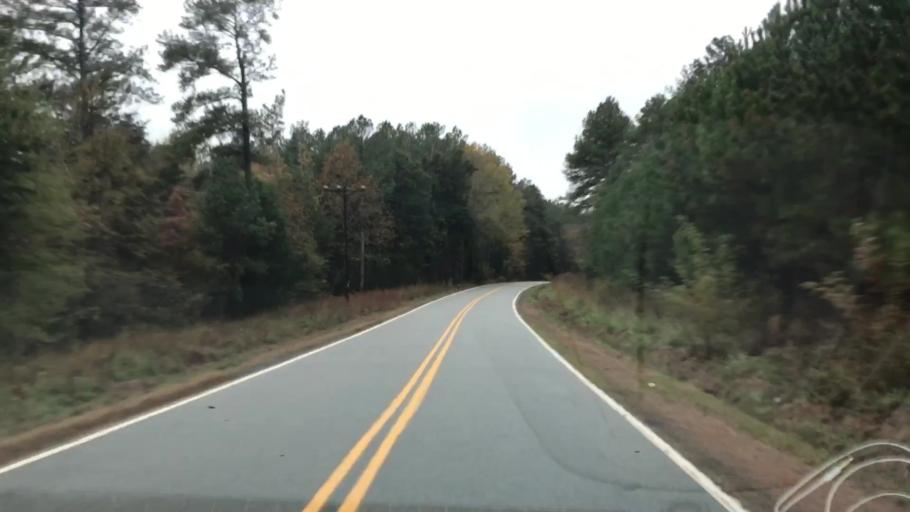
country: US
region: South Carolina
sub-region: Greenwood County
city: Ninety Six
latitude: 34.3073
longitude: -81.9612
